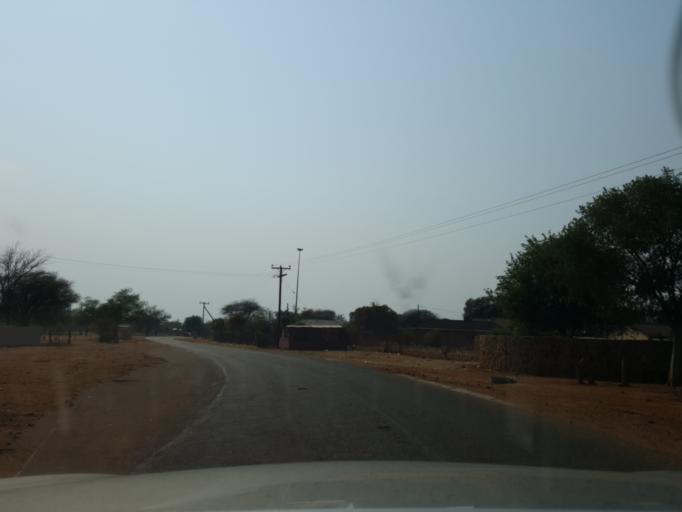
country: BW
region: South East
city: Lobatse
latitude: -25.2879
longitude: 25.9002
